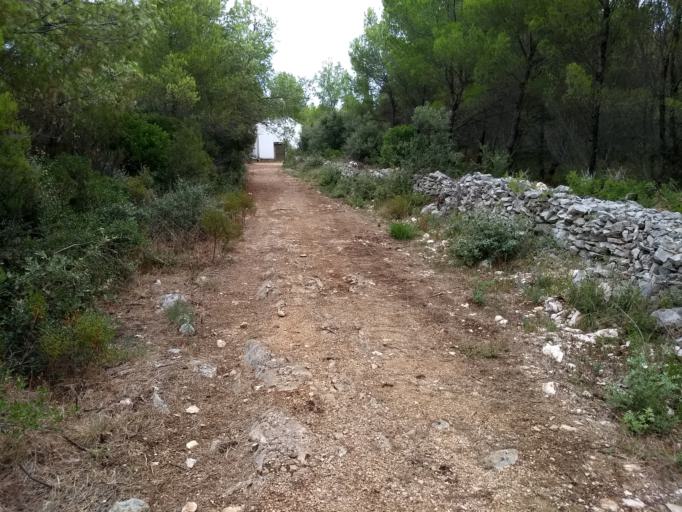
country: HR
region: Zadarska
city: Ugljan
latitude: 44.1434
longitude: 15.0793
